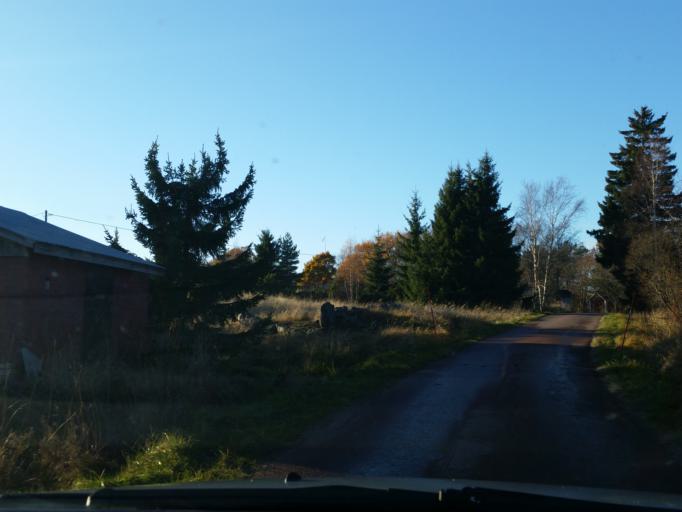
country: AX
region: Alands skaergard
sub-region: Braendoe
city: Braendoe
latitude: 60.3571
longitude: 21.0679
